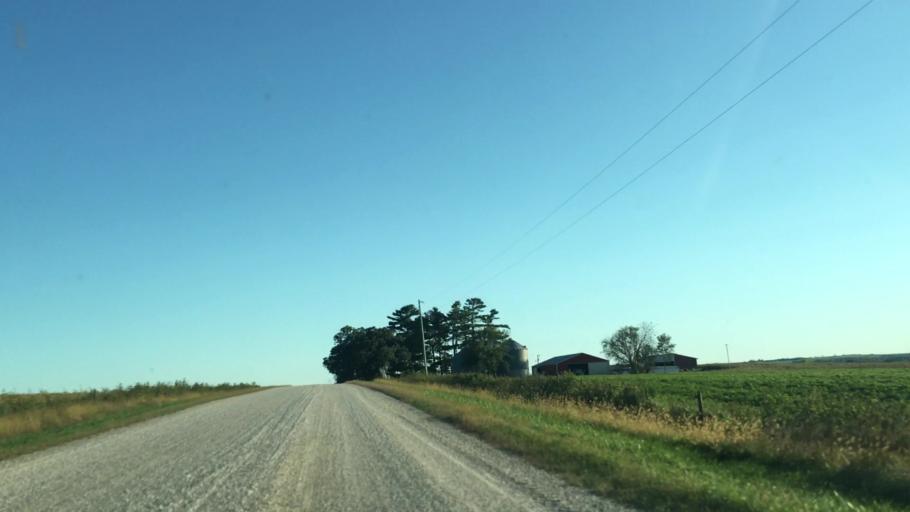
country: US
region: Minnesota
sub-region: Fillmore County
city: Preston
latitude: 43.8101
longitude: -92.0396
